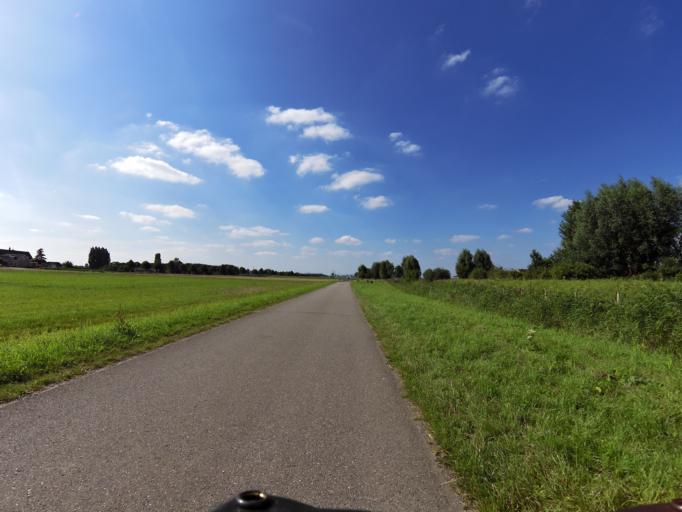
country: NL
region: South Holland
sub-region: Gemeente Binnenmaas
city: Heinenoord
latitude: 51.8542
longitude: 4.4661
